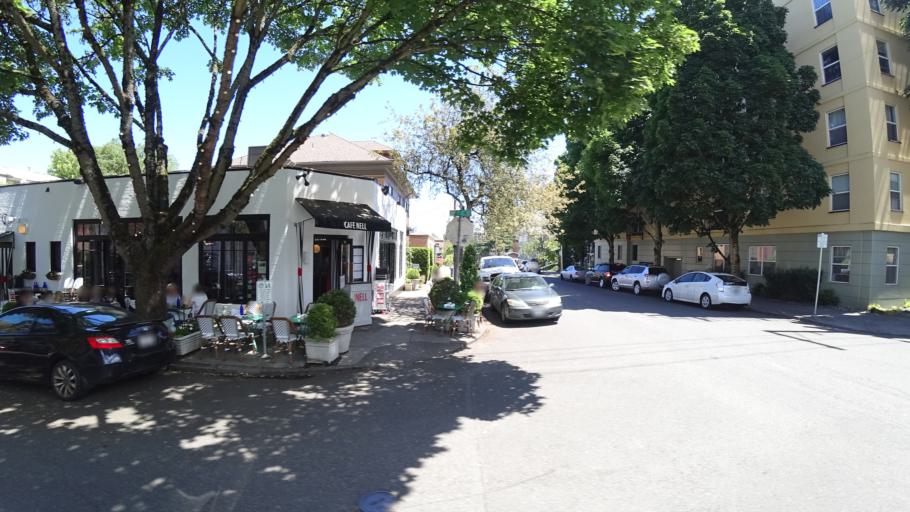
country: US
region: Oregon
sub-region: Multnomah County
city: Portland
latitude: 45.5293
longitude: -122.6926
